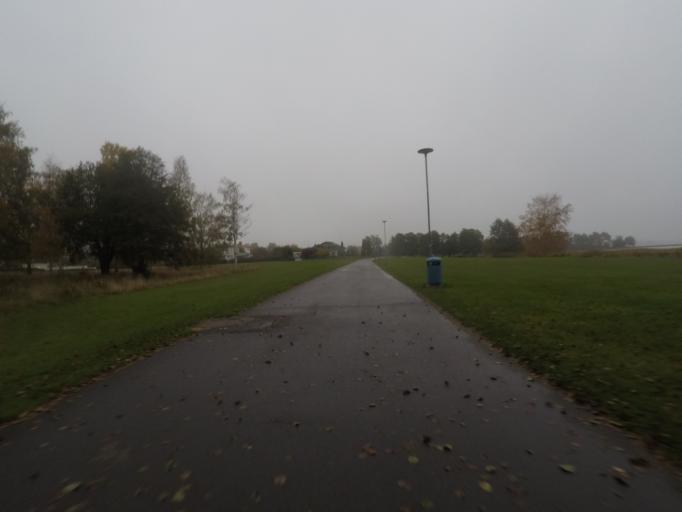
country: SE
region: OErebro
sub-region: Karlskoga Kommun
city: Karlskoga
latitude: 59.3175
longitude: 14.5166
